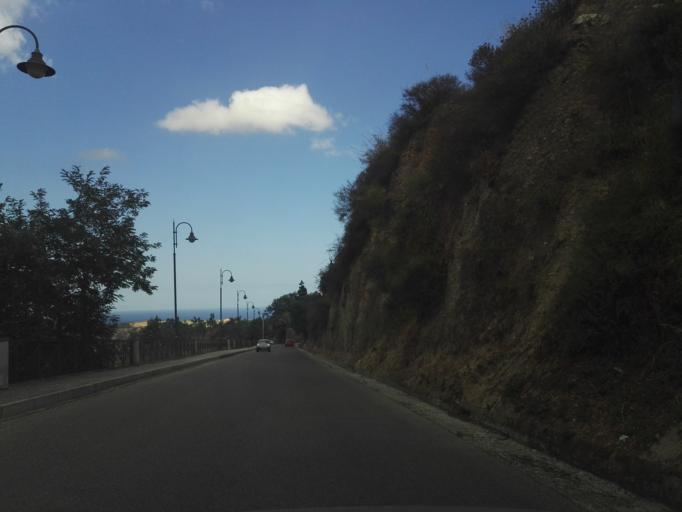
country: IT
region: Calabria
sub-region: Provincia di Reggio Calabria
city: Riace
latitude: 38.4149
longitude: 16.4847
